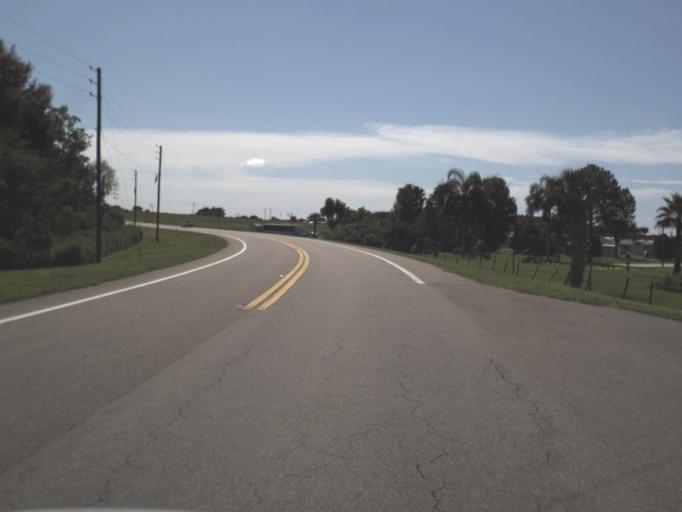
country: US
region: Florida
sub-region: Polk County
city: Polk City
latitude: 28.1684
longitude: -81.8066
